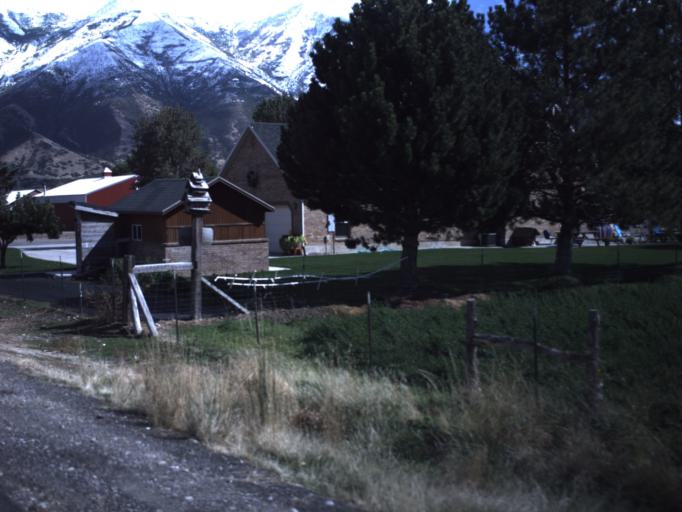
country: US
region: Utah
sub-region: Utah County
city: Mapleton
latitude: 40.1155
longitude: -111.6048
